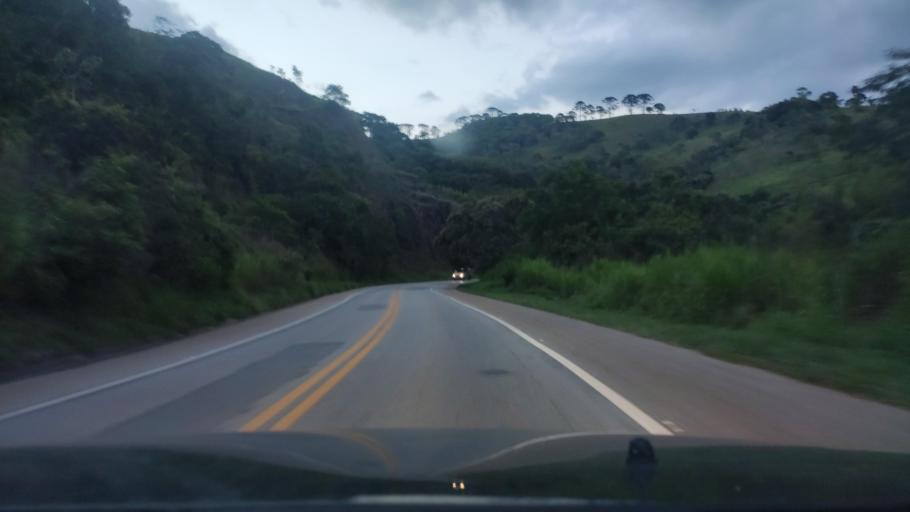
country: BR
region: Sao Paulo
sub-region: Campos Do Jordao
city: Campos do Jordao
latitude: -22.8000
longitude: -45.7492
